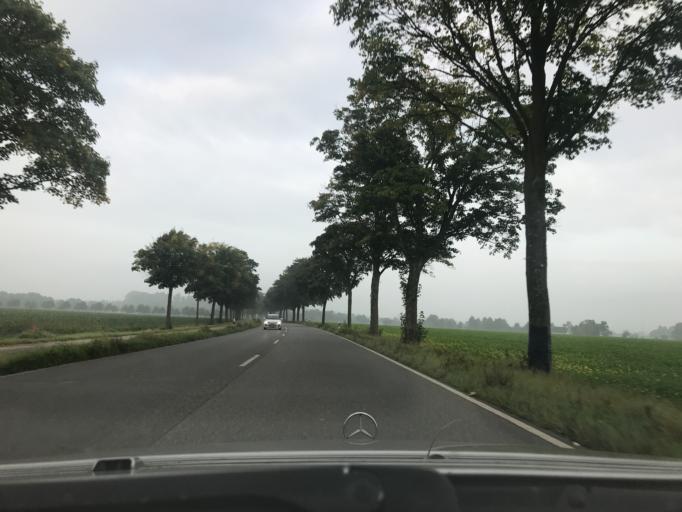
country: DE
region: North Rhine-Westphalia
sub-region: Regierungsbezirk Dusseldorf
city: Moers
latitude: 51.4151
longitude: 6.5683
